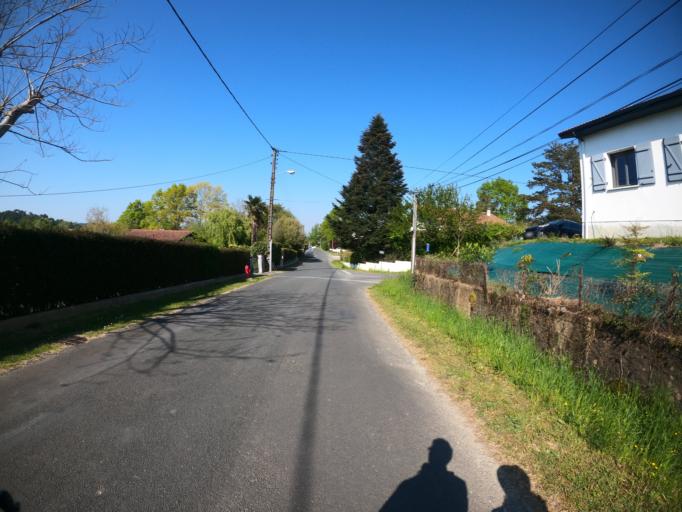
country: FR
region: Aquitaine
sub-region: Departement des Pyrenees-Atlantiques
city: Bassussarry
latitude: 43.4399
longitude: -1.5002
